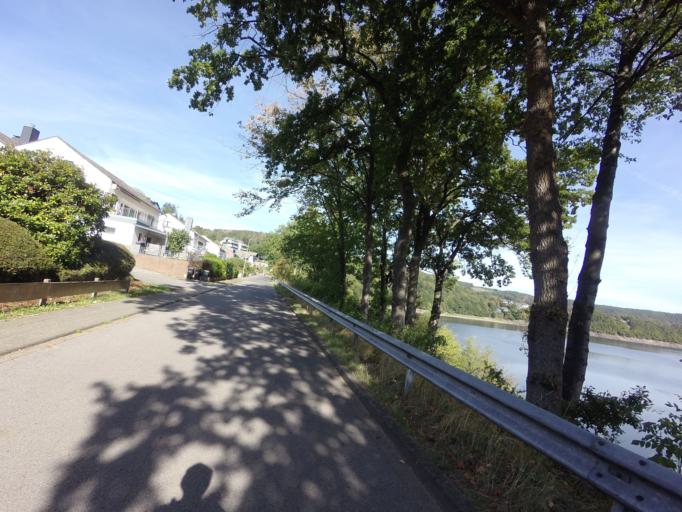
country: DE
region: North Rhine-Westphalia
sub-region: Regierungsbezirk Koln
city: Simmerath
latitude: 50.6189
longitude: 6.3820
